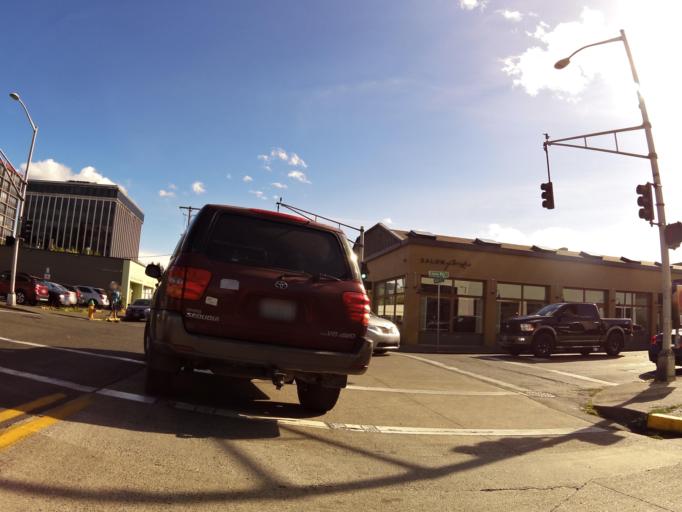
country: US
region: Washington
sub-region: Thurston County
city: Olympia
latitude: 47.0434
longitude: -122.9027
